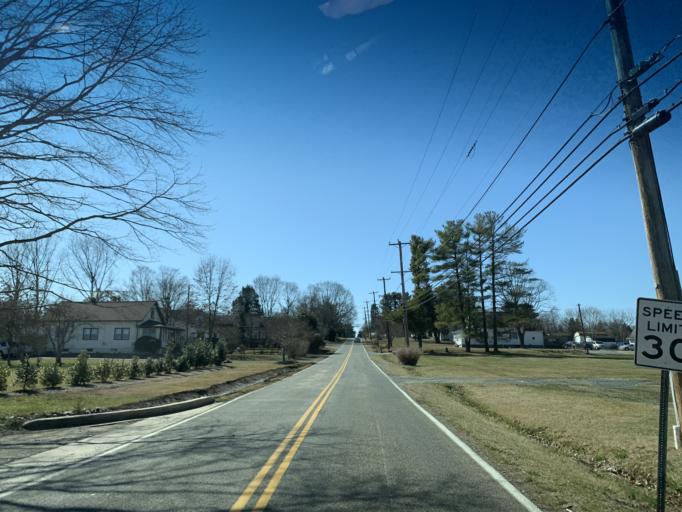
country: US
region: Maryland
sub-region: Cecil County
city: Elkton
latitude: 39.5221
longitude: -75.8188
